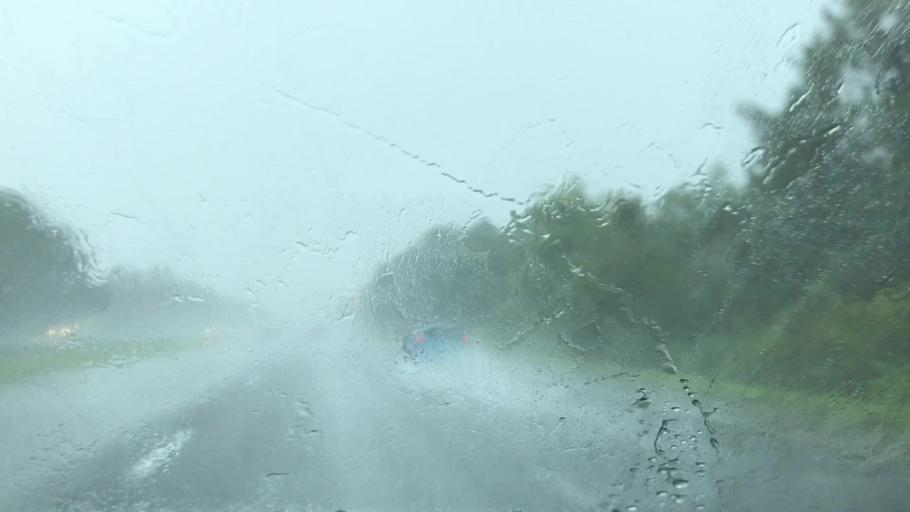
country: US
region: Florida
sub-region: Volusia County
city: Ormond-by-the-Sea
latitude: 29.3625
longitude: -81.1374
